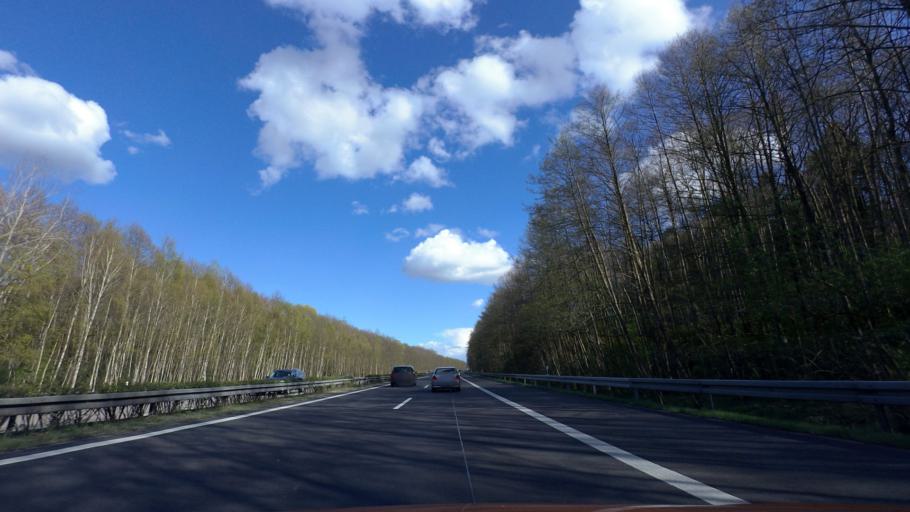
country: DE
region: Brandenburg
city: Putlitz
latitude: 53.2898
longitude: 12.0593
